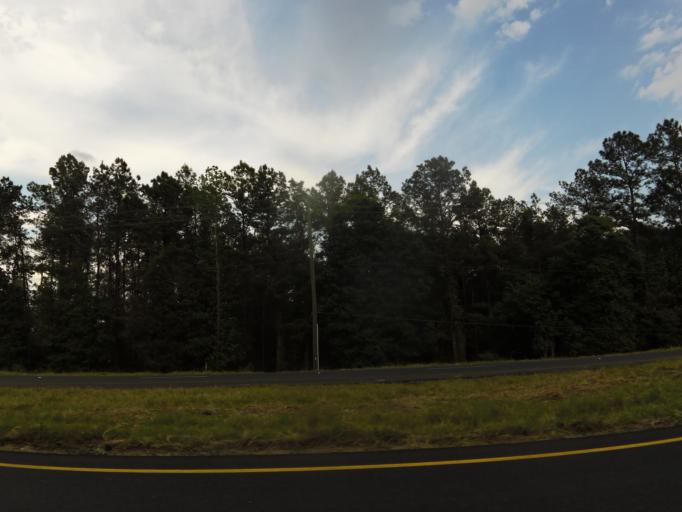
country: US
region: Georgia
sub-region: Charlton County
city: Folkston
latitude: 30.8042
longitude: -81.9928
